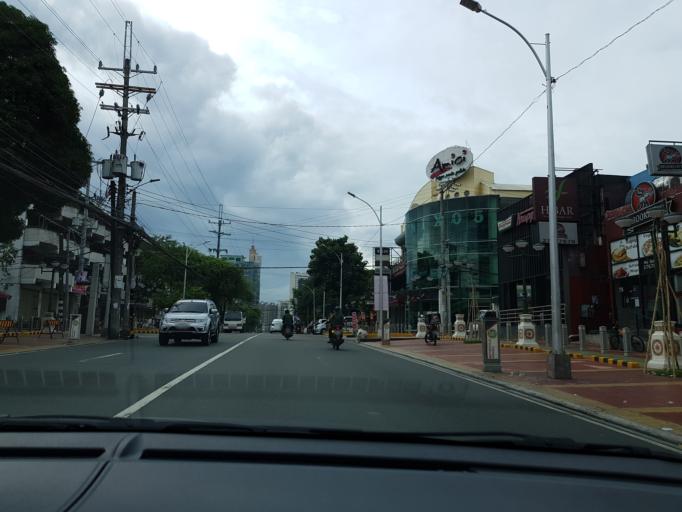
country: PH
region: Calabarzon
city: Del Monte
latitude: 14.6327
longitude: 121.0348
